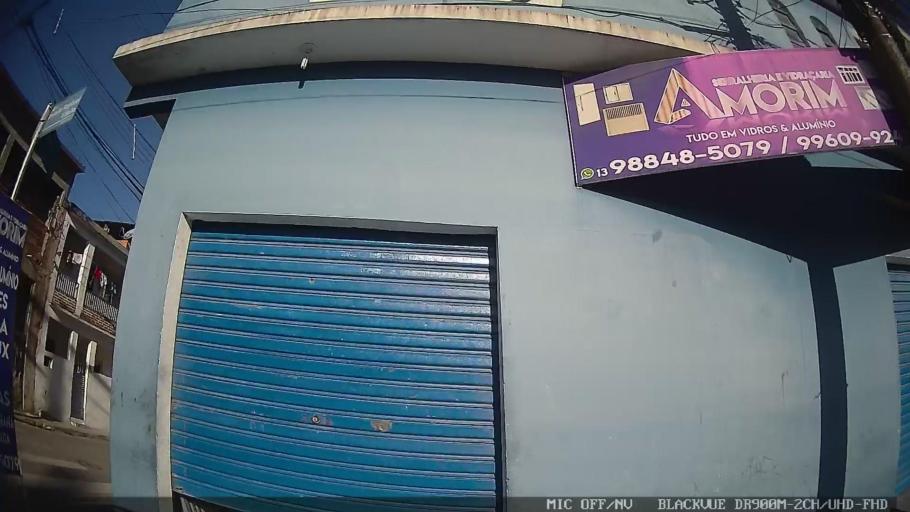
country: BR
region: Sao Paulo
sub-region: Guaruja
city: Guaruja
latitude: -23.9689
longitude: -46.2452
